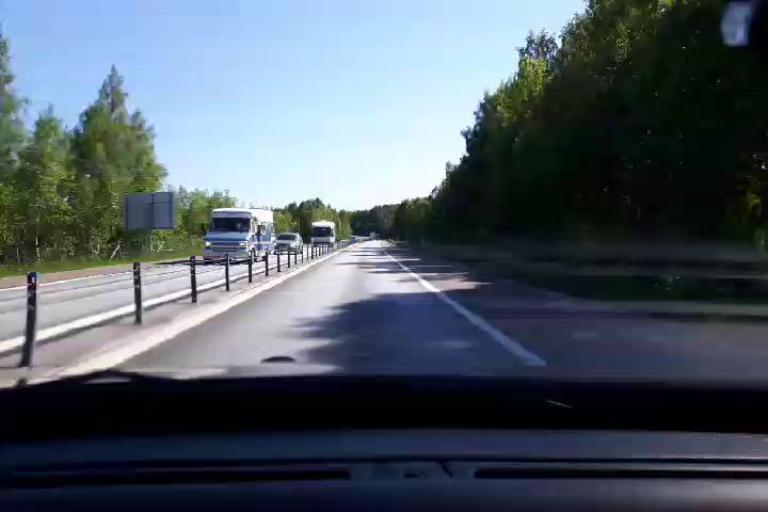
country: SE
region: Gaevleborg
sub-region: Soderhamns Kommun
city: Soderhamn
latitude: 61.2772
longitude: 17.0270
